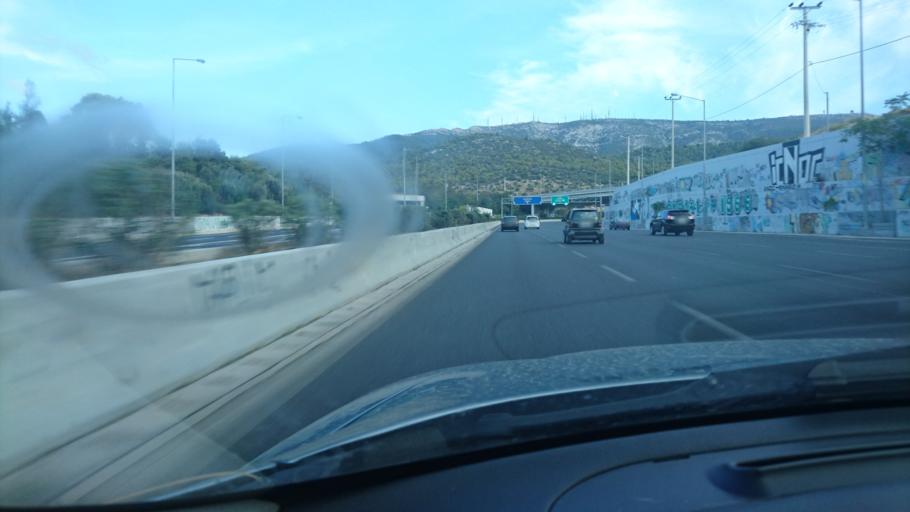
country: GR
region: Attica
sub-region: Nomos Attikis
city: Zografos
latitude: 37.9750
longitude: 23.7909
